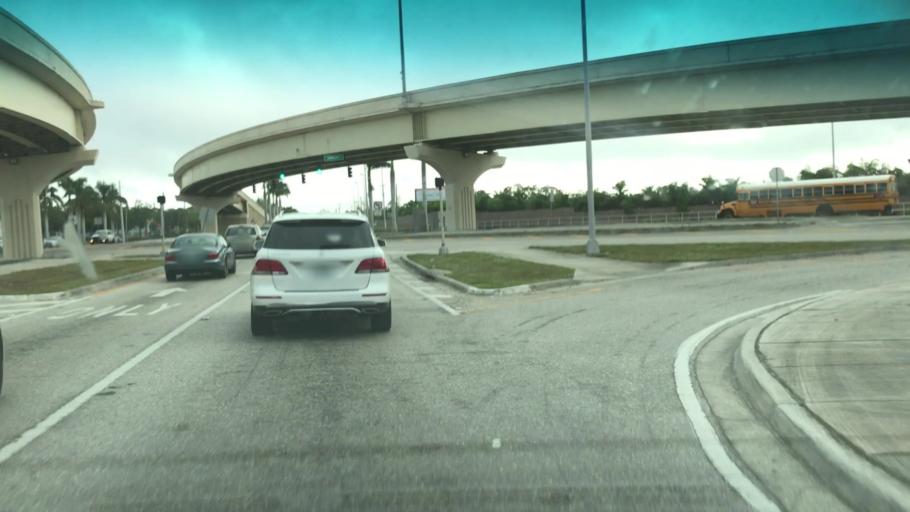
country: US
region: Florida
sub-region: Lee County
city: Cypress Lake
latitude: 26.5206
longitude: -81.8920
